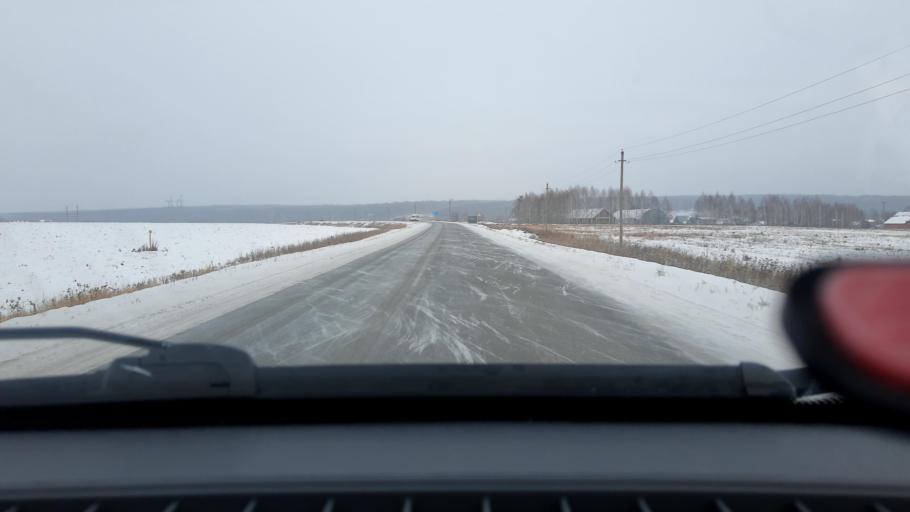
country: RU
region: Bashkortostan
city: Iglino
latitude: 54.7506
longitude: 56.4000
